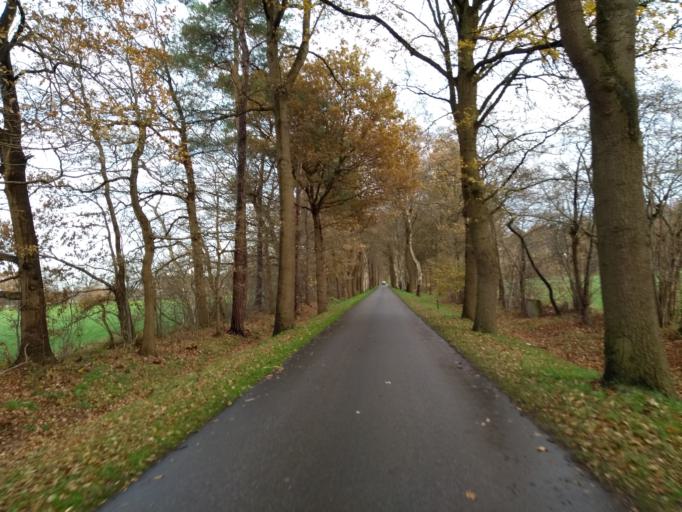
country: NL
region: Overijssel
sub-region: Gemeente Almelo
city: Almelo
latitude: 52.3572
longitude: 6.7145
